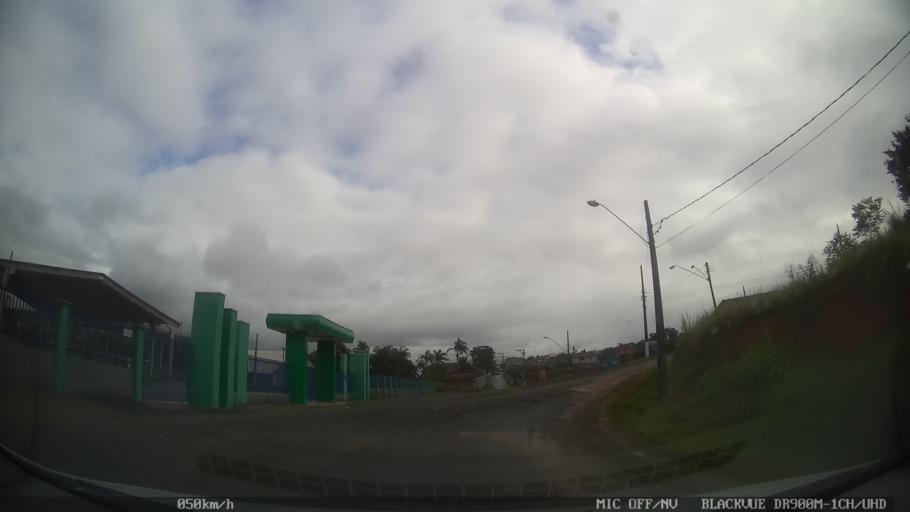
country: BR
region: Sao Paulo
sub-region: Cajati
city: Cajati
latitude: -24.7236
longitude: -48.1015
